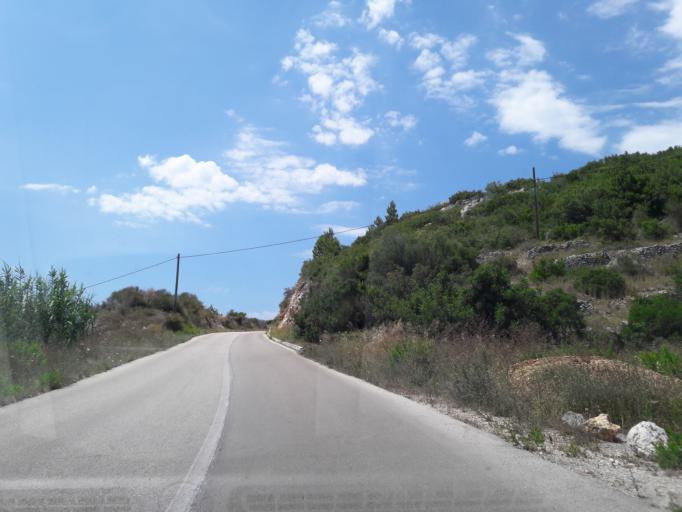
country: HR
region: Dubrovacko-Neretvanska
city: Korcula
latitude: 42.9792
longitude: 17.1266
